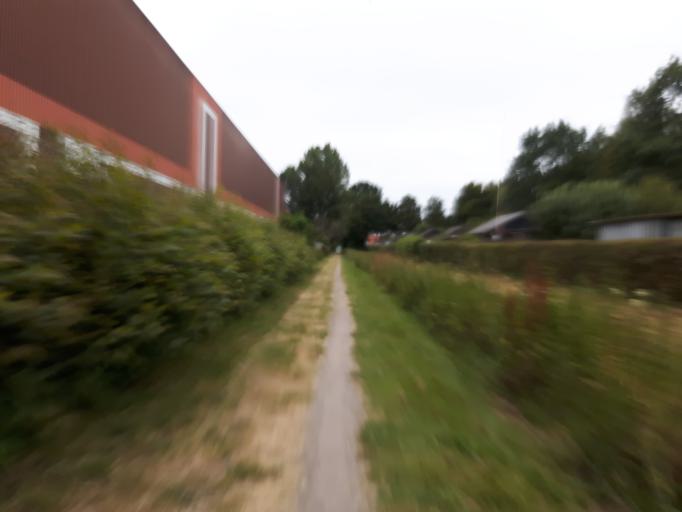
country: DE
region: Lower Saxony
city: Delmenhorst
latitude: 53.0198
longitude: 8.6611
